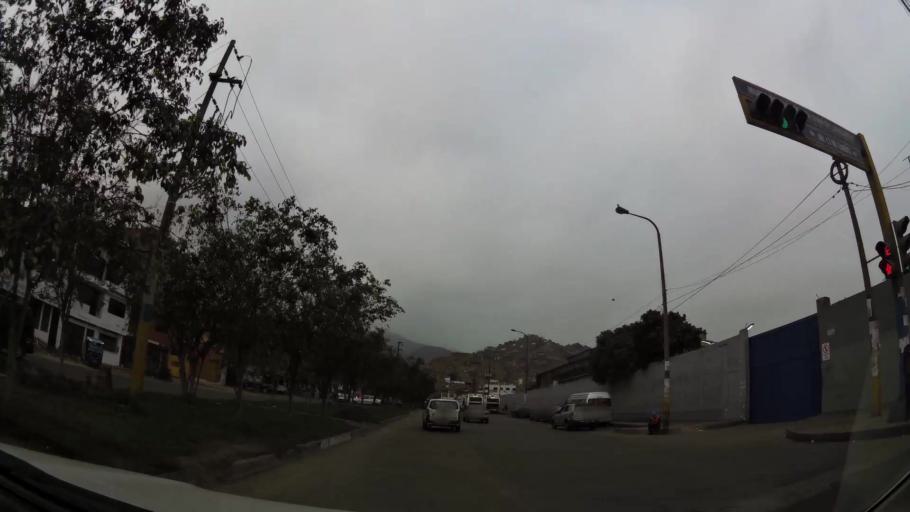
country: PE
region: Lima
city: Lima
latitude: -12.0114
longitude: -76.9984
